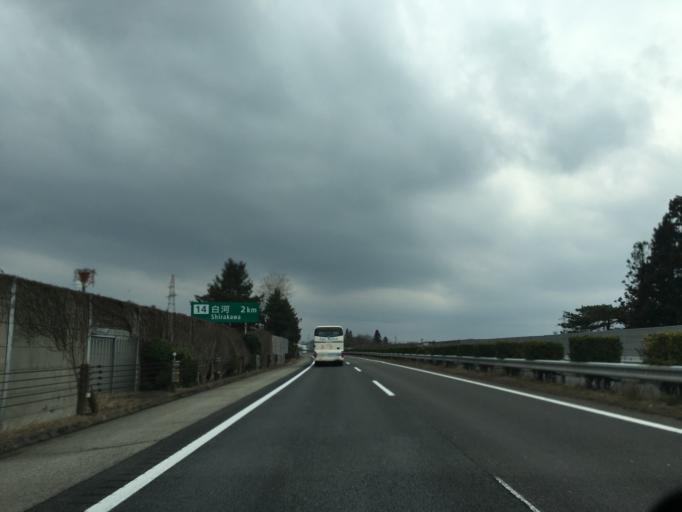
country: JP
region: Tochigi
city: Kuroiso
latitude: 37.1309
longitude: 140.1809
